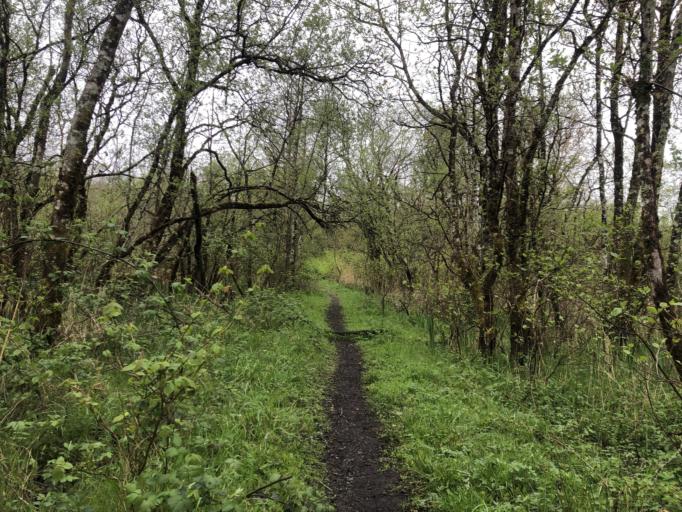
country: IE
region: Connaught
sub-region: County Leitrim
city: Carrick-on-Shannon
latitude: 53.9875
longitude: -8.1792
